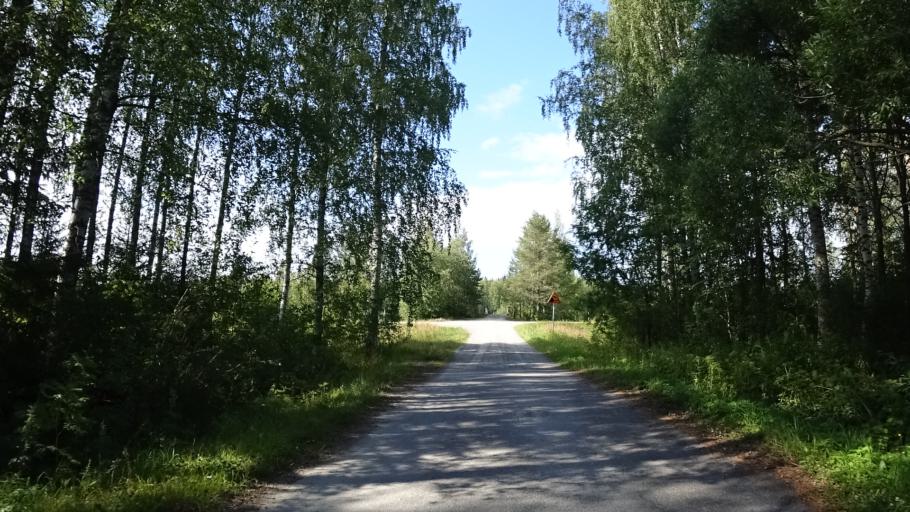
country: FI
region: North Karelia
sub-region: Joensuu
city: Eno
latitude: 62.8006
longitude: 30.1490
